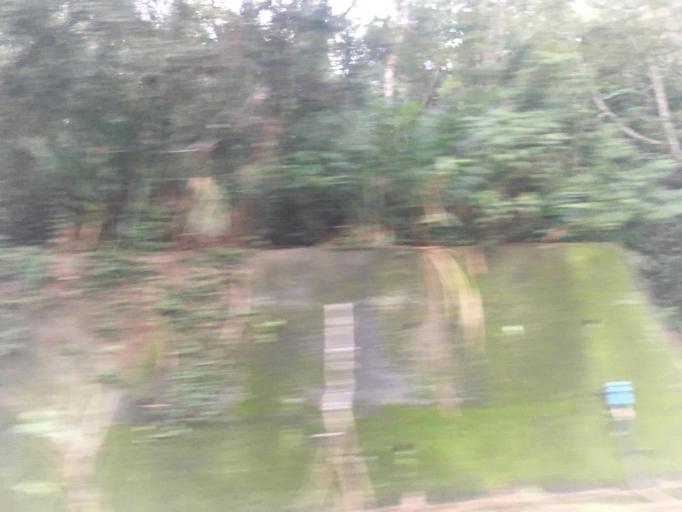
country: TW
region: Taiwan
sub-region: Miaoli
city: Miaoli
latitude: 24.4256
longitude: 120.7637
